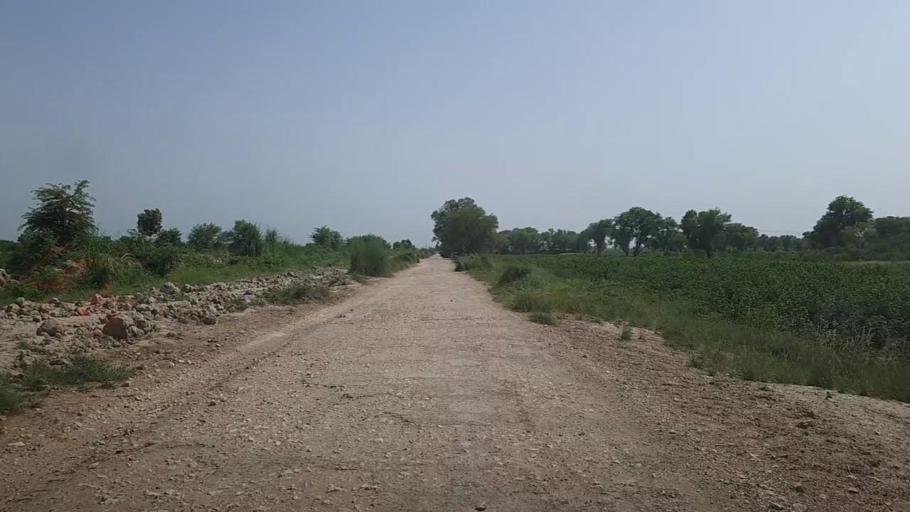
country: PK
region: Sindh
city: Pad Idan
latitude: 26.7888
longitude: 68.3265
